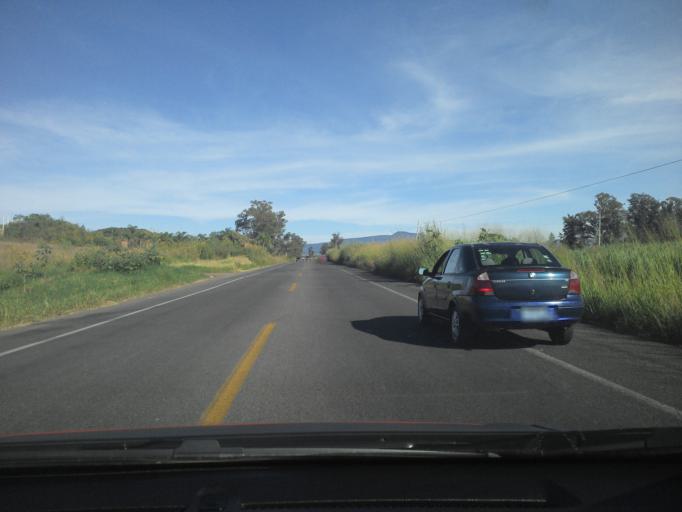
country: MX
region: Jalisco
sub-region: Teuchitlan
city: La Estanzuela
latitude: 20.6674
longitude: -103.7909
